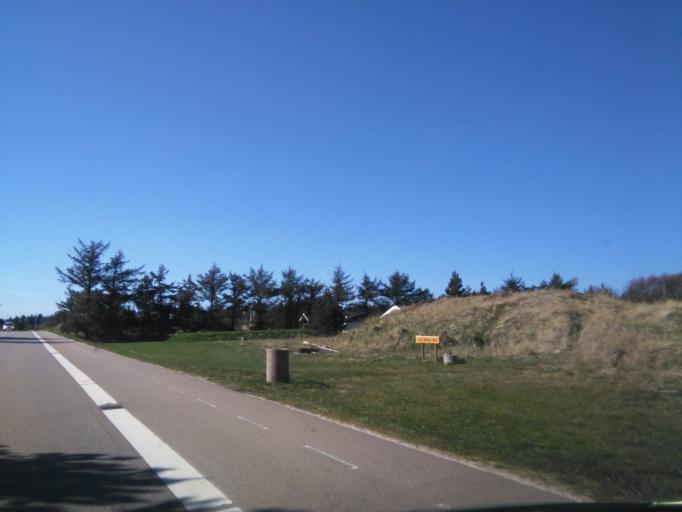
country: DK
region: South Denmark
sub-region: Varde Kommune
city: Oksbol
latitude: 55.5492
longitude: 8.1525
